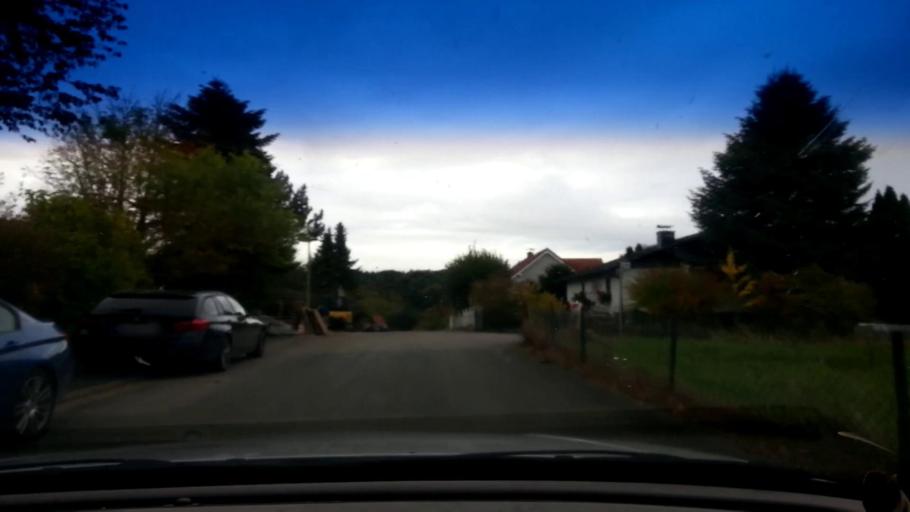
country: DE
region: Bavaria
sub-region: Upper Franconia
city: Priesendorf
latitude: 49.9047
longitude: 10.7169
